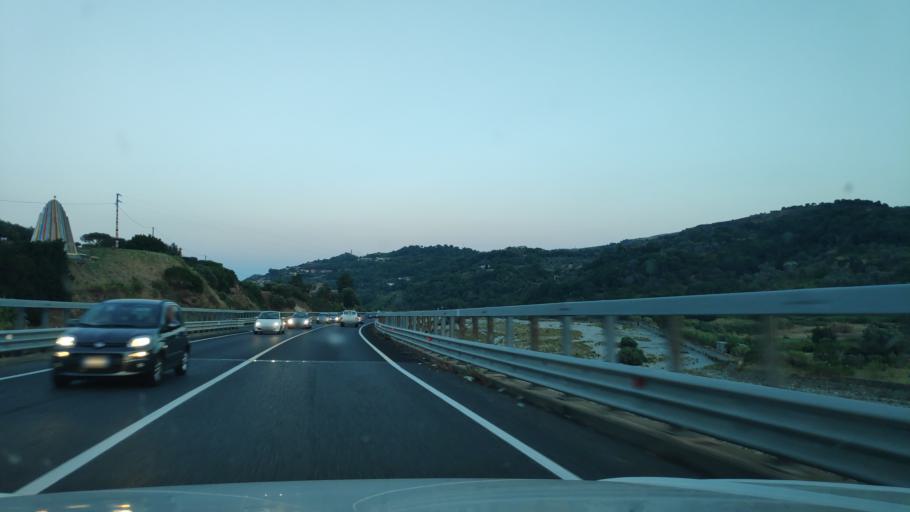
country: IT
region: Calabria
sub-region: Provincia di Reggio Calabria
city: Grotteria
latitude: 38.3491
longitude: 16.2550
